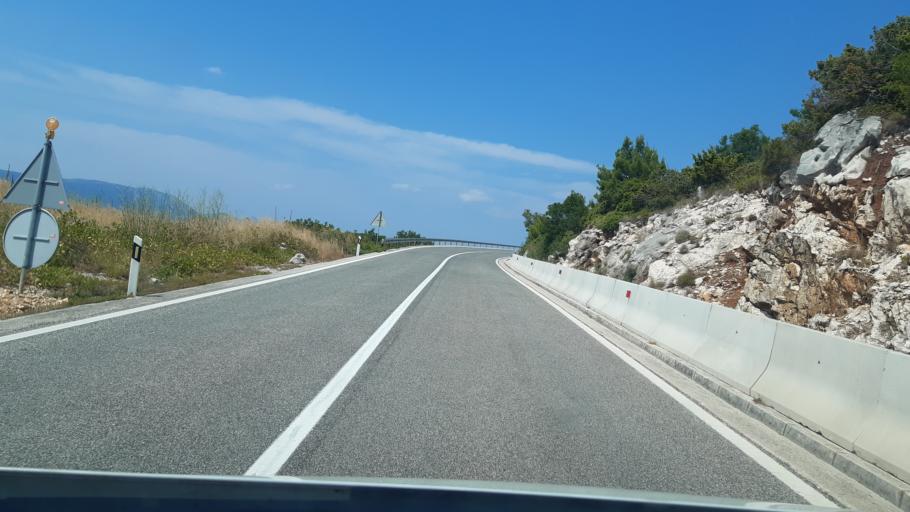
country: HR
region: Dubrovacko-Neretvanska
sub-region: Grad Dubrovnik
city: Opuzen
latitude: 42.9589
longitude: 17.5253
